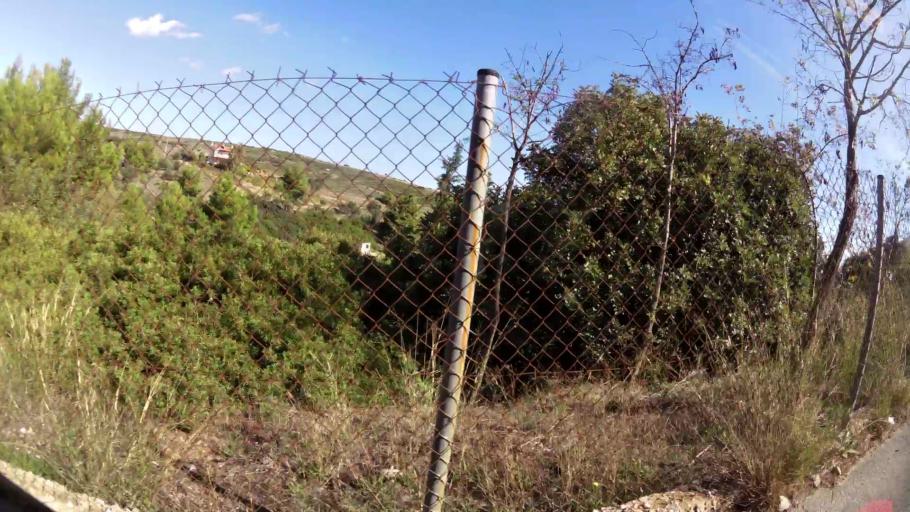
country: GR
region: Attica
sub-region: Nomarchia Anatolikis Attikis
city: Dioni
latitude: 38.0123
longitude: 23.9336
